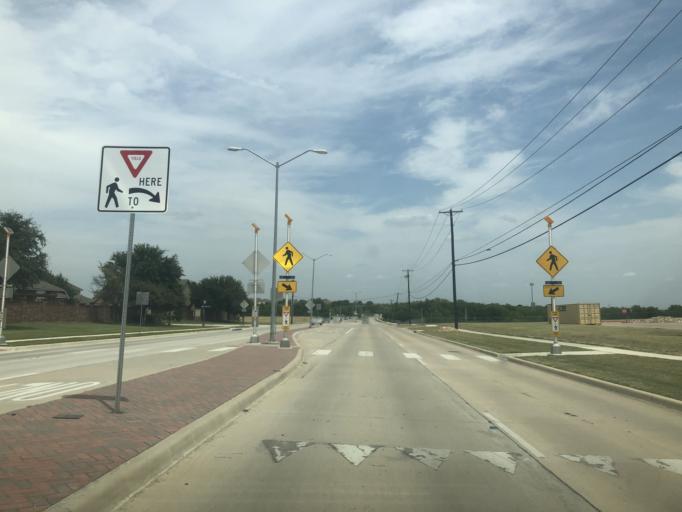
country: US
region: Texas
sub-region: Tarrant County
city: Saginaw
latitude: 32.8837
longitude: -97.3478
